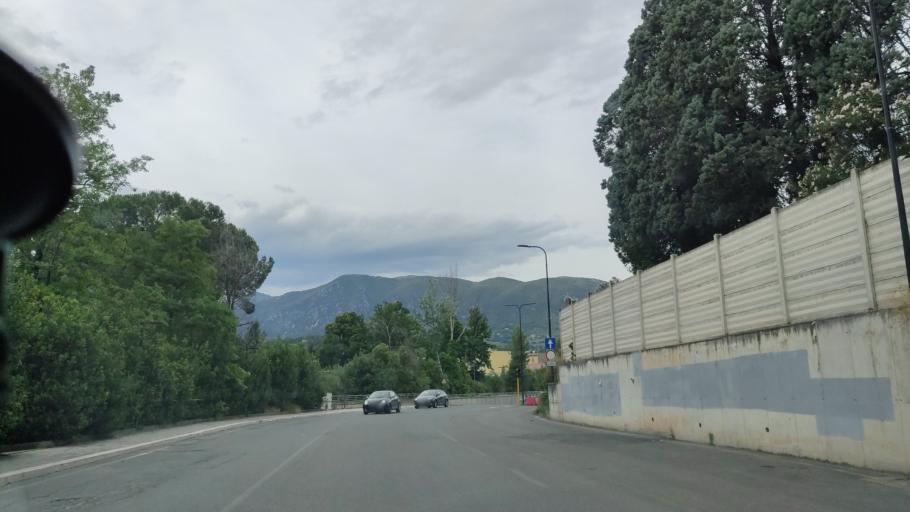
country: IT
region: Umbria
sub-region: Provincia di Terni
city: Terni
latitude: 42.5653
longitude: 12.6590
